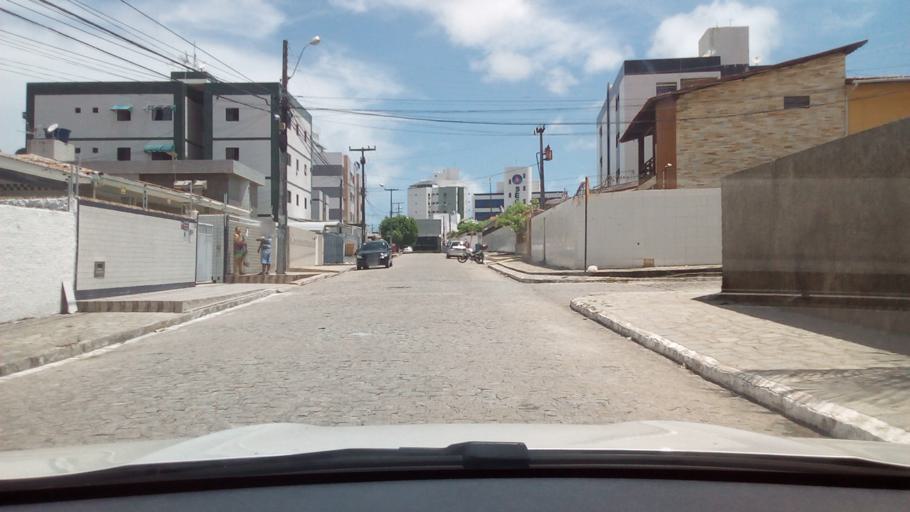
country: BR
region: Paraiba
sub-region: Joao Pessoa
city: Joao Pessoa
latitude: -7.1526
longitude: -34.8403
